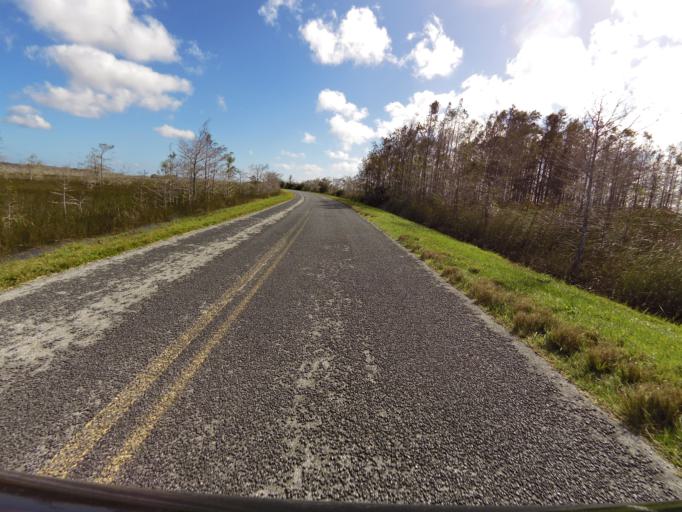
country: US
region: Florida
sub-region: Miami-Dade County
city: Florida City
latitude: 25.4351
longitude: -80.7811
